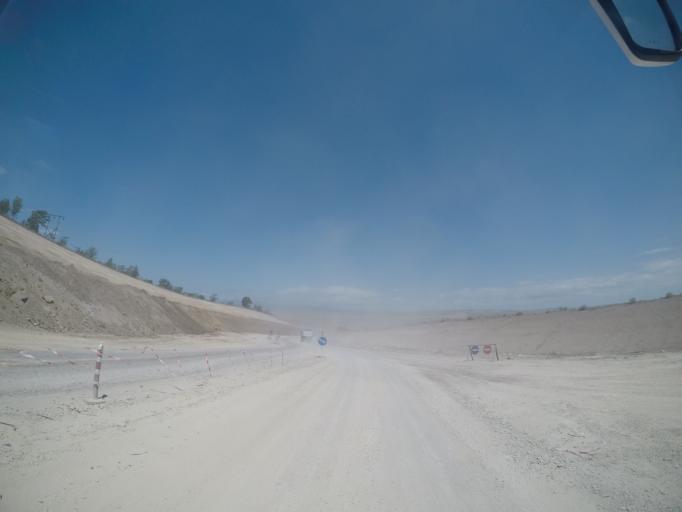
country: AZ
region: Qobustan
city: Qobustan
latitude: 40.5368
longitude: 48.7760
